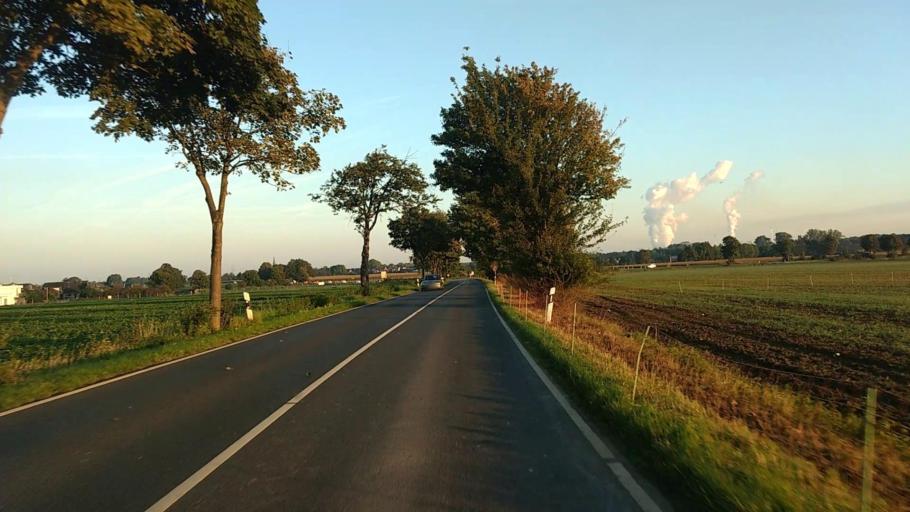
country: DE
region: North Rhine-Westphalia
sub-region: Regierungsbezirk Koln
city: Bergheim
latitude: 50.9295
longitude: 6.6430
